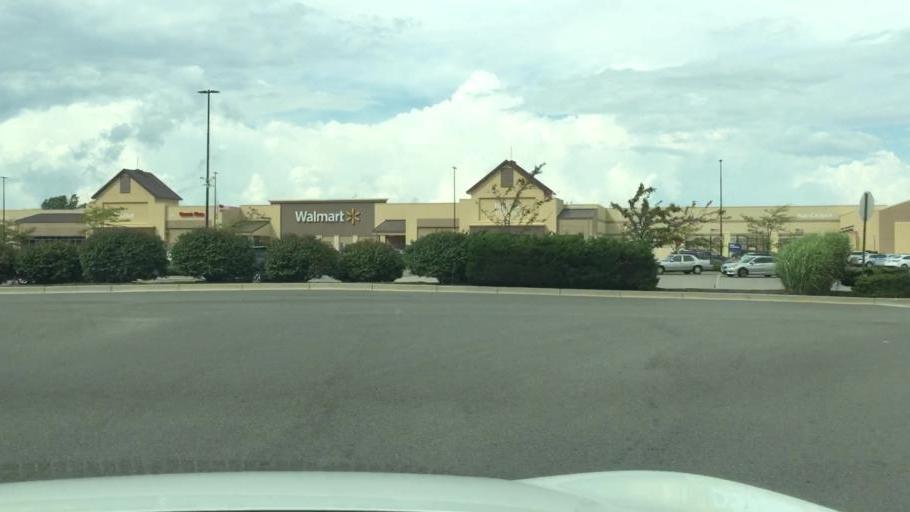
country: US
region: Ohio
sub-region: Champaign County
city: Urbana
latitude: 40.1067
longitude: -83.7158
